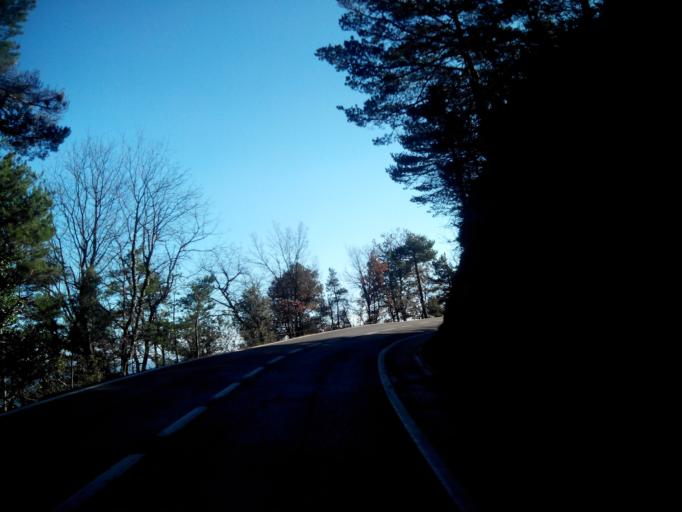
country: ES
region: Catalonia
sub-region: Provincia de Barcelona
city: Berga
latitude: 42.0970
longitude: 1.8091
